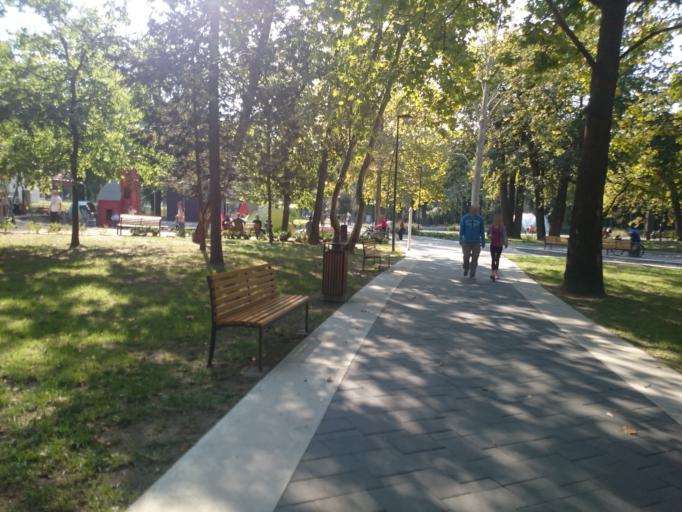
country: HU
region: Hajdu-Bihar
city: Debrecen
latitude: 47.5527
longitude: 21.6273
